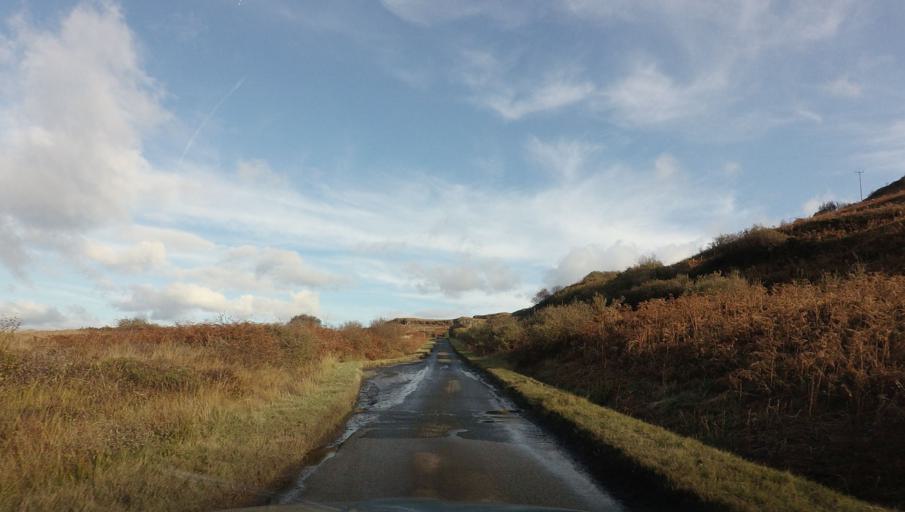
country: GB
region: Scotland
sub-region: Argyll and Bute
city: Isle Of Mull
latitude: 56.3399
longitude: -6.1343
